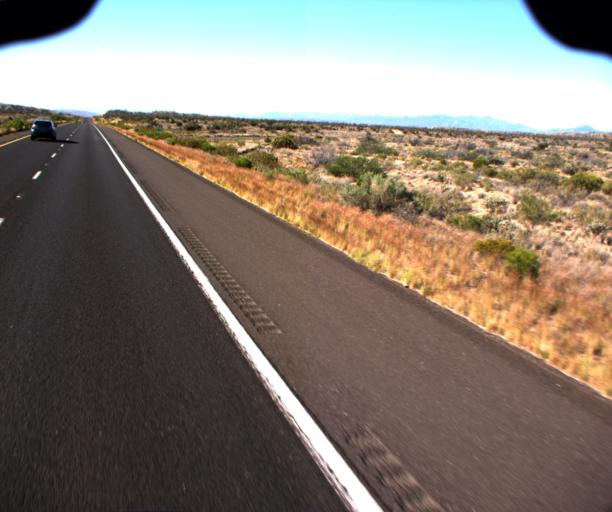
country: US
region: Arizona
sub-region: Mohave County
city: Kingman
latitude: 35.1000
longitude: -113.6665
